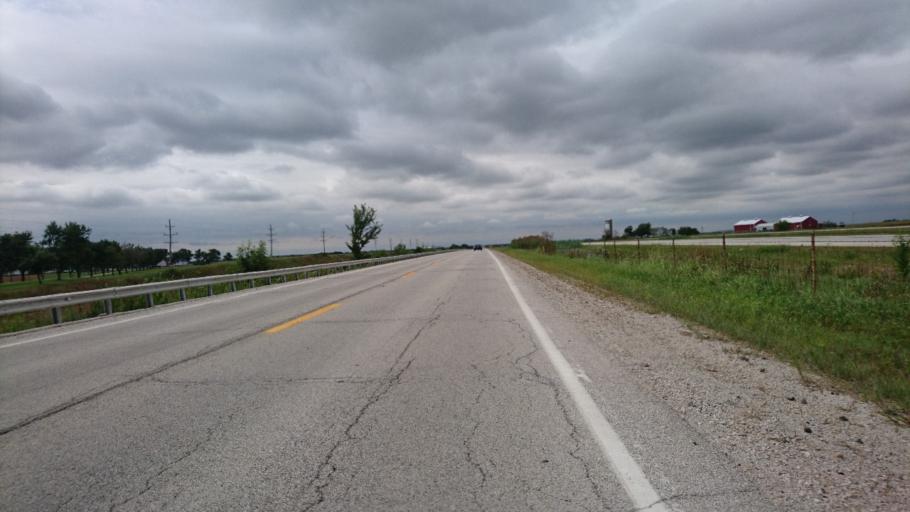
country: US
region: Illinois
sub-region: Livingston County
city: Odell
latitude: 40.9760
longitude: -88.5508
